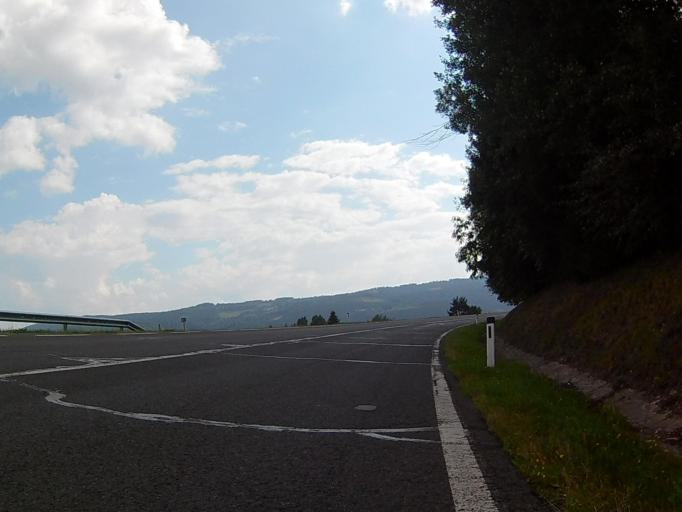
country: AT
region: Styria
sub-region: Politischer Bezirk Deutschlandsberg
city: Soboth
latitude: 46.6815
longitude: 15.0525
